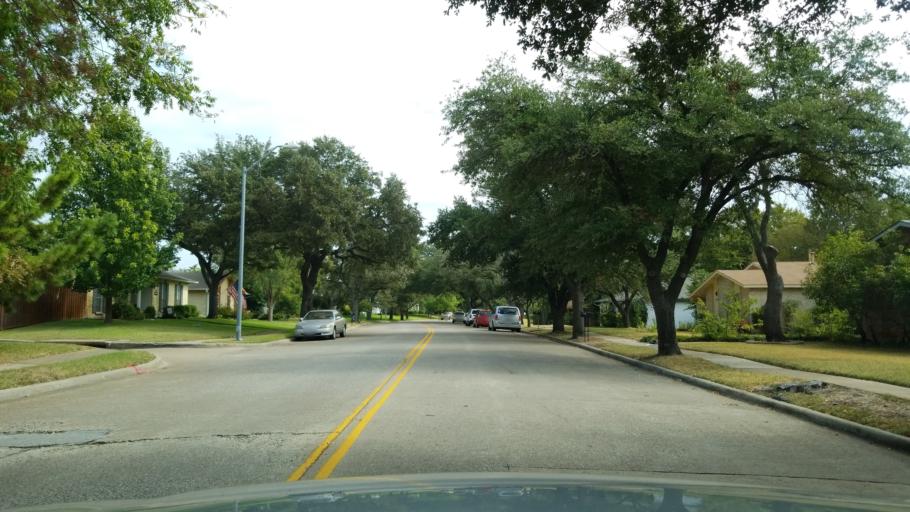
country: US
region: Texas
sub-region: Dallas County
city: Garland
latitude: 32.8742
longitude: -96.6936
